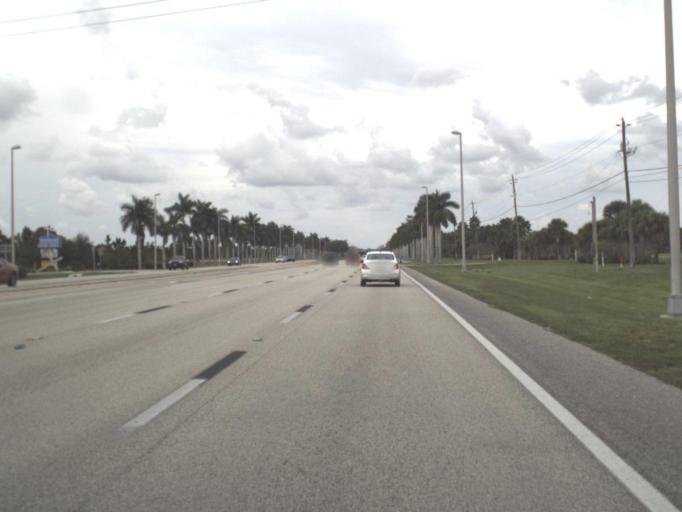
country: US
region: Florida
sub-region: Lee County
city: Fort Myers Shores
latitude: 26.6949
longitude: -81.7798
